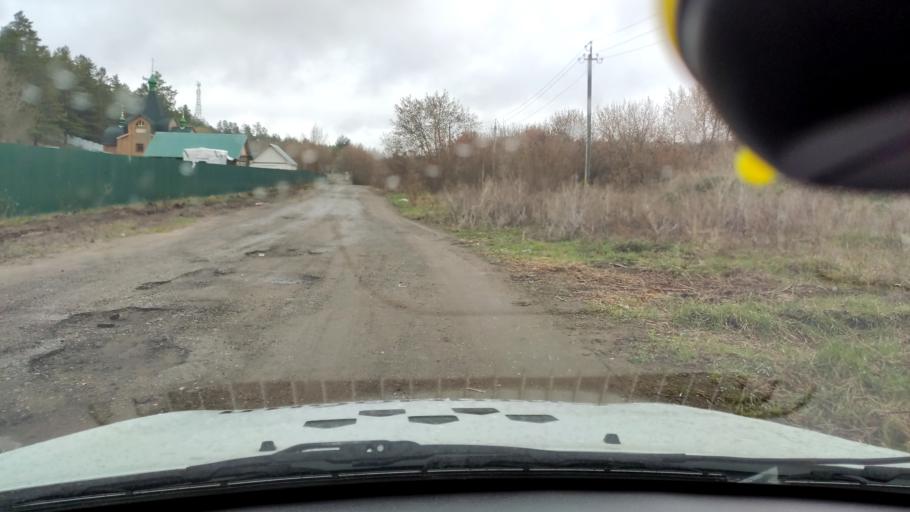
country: RU
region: Samara
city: Tol'yatti
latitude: 53.5251
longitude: 49.3926
